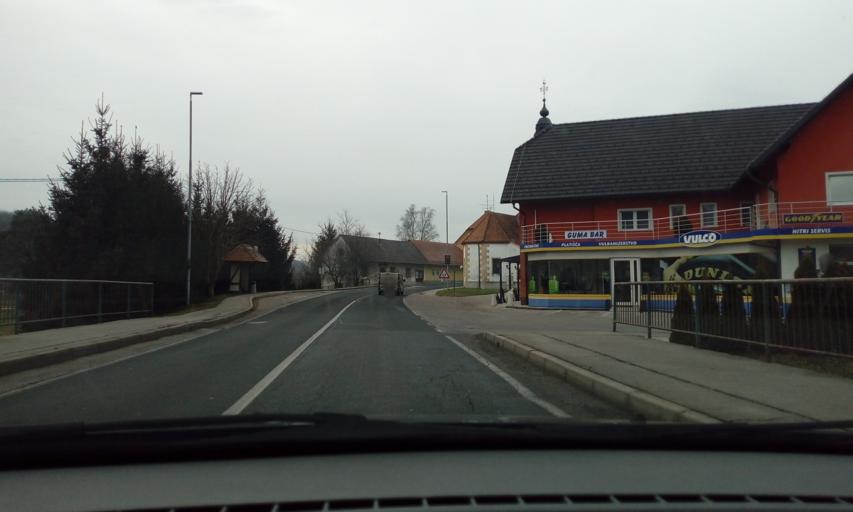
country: SI
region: Smarje pri Jelsah
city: Smarje pri Jelsah
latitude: 46.2268
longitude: 15.4680
